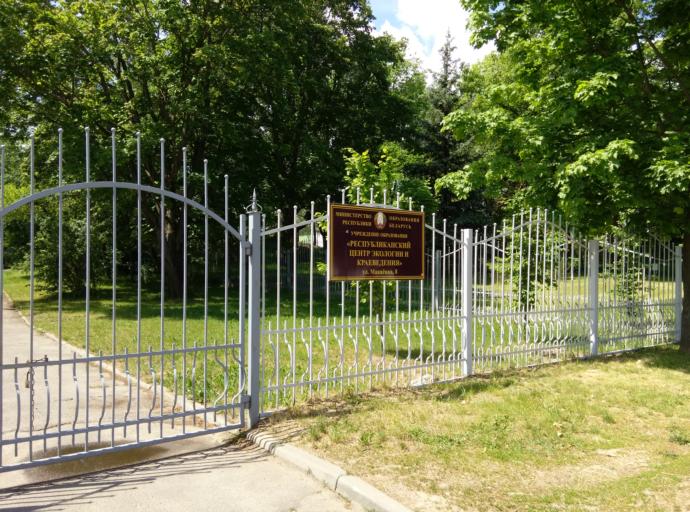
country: BY
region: Minsk
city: Minsk
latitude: 53.9253
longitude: 27.6281
